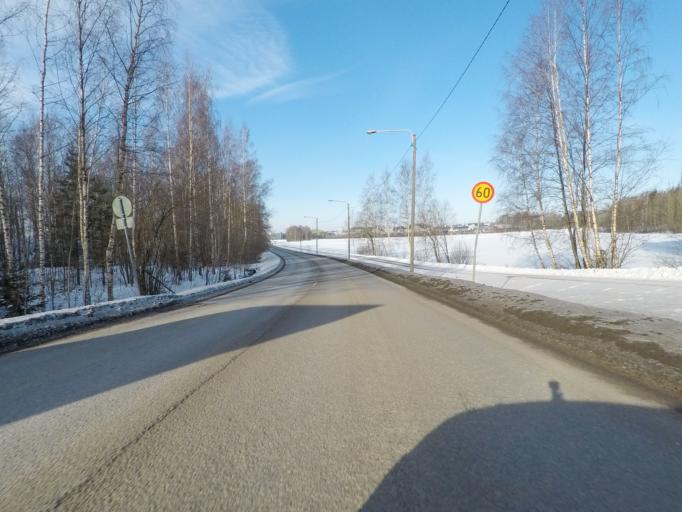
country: FI
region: Uusimaa
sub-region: Helsinki
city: Vantaa
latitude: 60.2199
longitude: 25.0418
